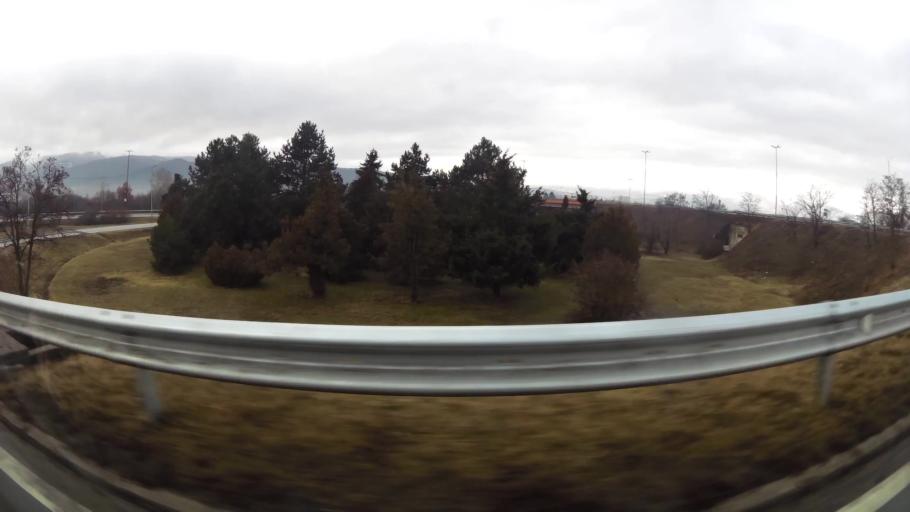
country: BG
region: Sofia-Capital
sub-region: Stolichna Obshtina
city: Sofia
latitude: 42.6342
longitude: 23.4497
